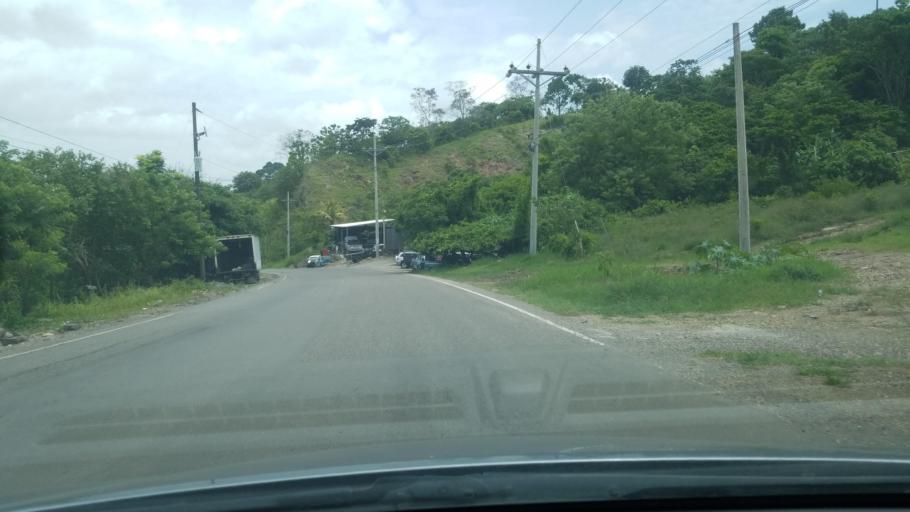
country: HN
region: Copan
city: Ojos de Agua
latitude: 14.6766
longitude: -88.8168
